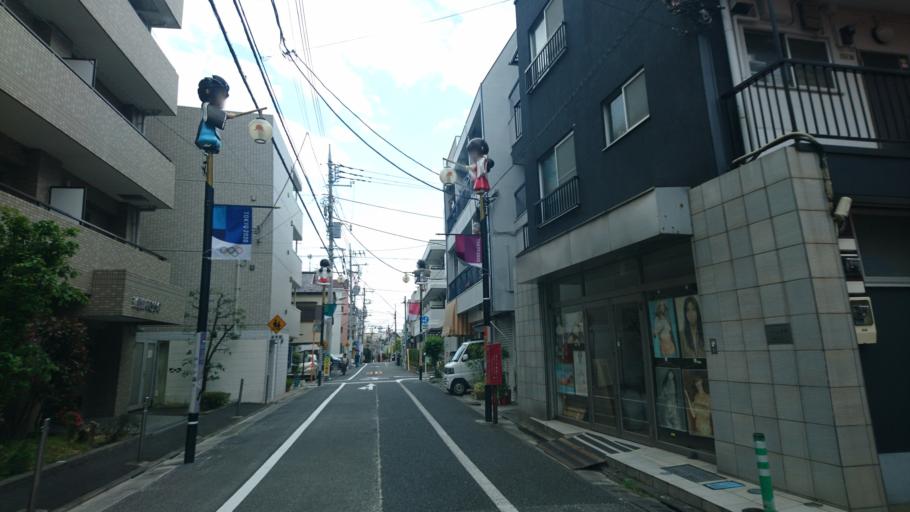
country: JP
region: Kanagawa
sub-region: Kawasaki-shi
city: Kawasaki
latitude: 35.6049
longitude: 139.7184
